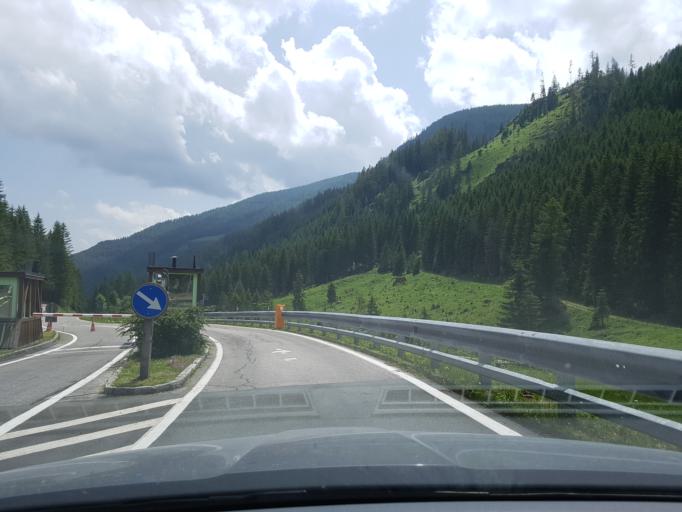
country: AT
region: Carinthia
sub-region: Politischer Bezirk Spittal an der Drau
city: Kleinkirchheim
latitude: 46.8846
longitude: 13.8500
